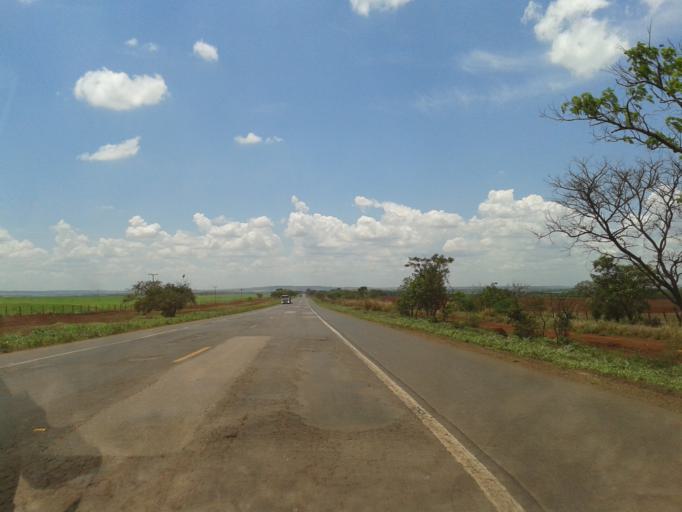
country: BR
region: Goias
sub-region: Goiatuba
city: Goiatuba
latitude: -18.2787
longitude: -49.6269
